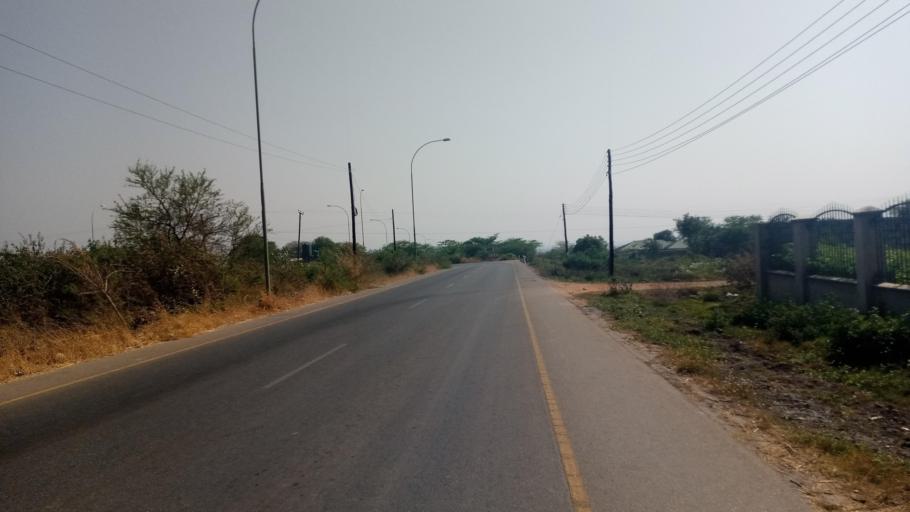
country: ZM
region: Lusaka
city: Lusaka
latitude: -15.4530
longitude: 28.4355
